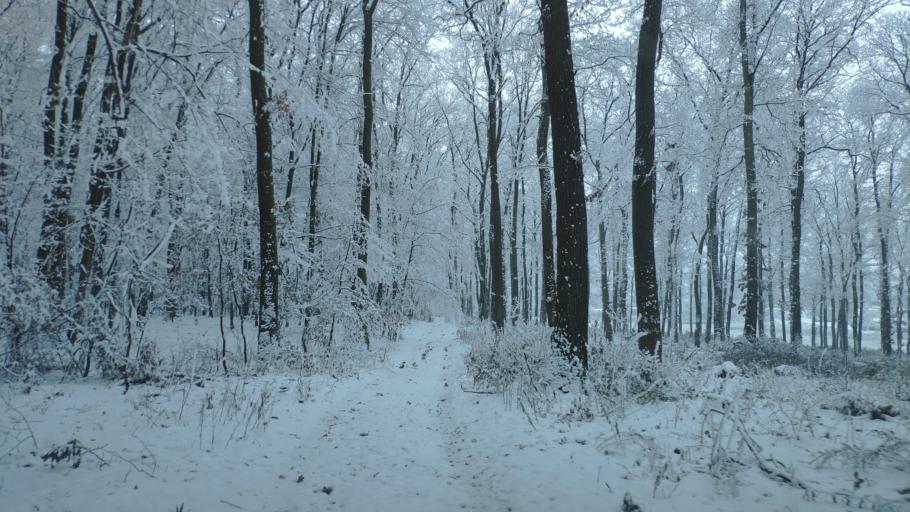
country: SK
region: Kosicky
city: Kosice
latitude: 48.6470
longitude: 21.1744
